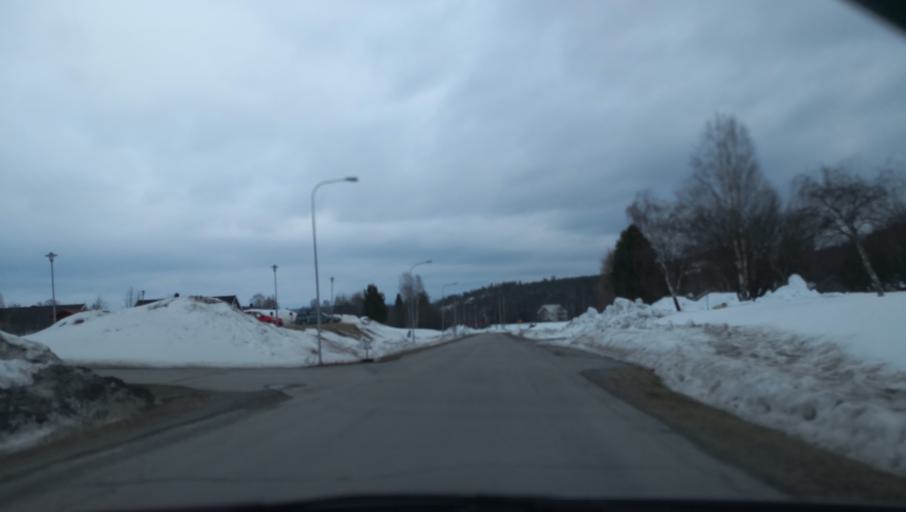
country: SE
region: Vaesterbotten
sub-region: Vannas Kommun
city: Vannasby
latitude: 63.9182
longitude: 19.8092
